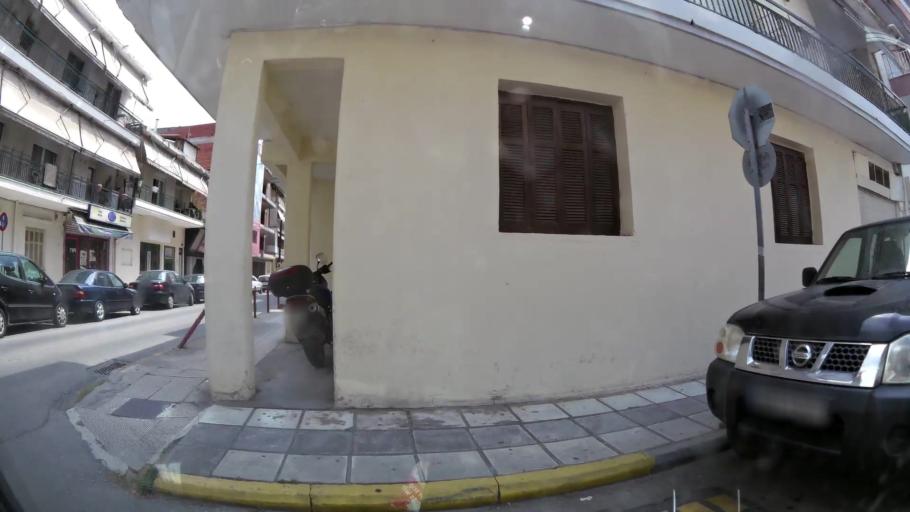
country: GR
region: Central Macedonia
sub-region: Nomos Pierias
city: Katerini
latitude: 40.2711
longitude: 22.5018
